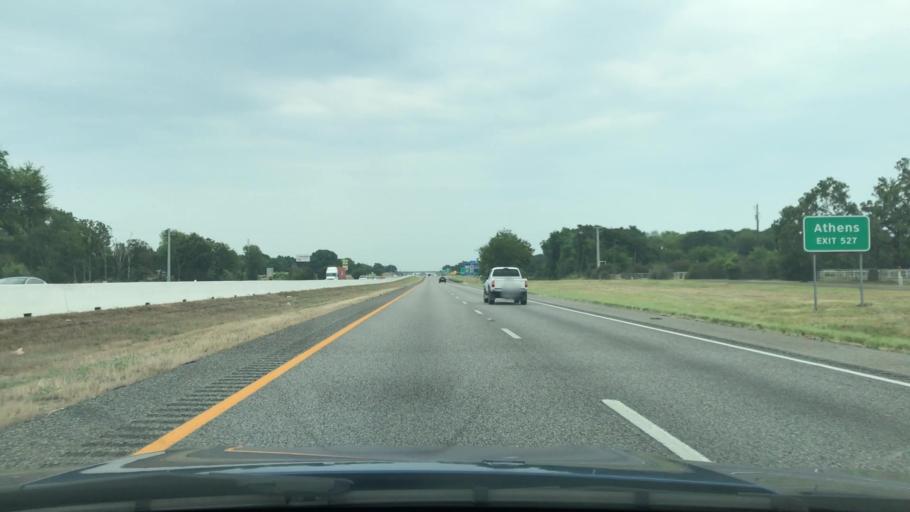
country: US
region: Texas
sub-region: Van Zandt County
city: Canton
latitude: 32.5898
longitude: -95.8834
